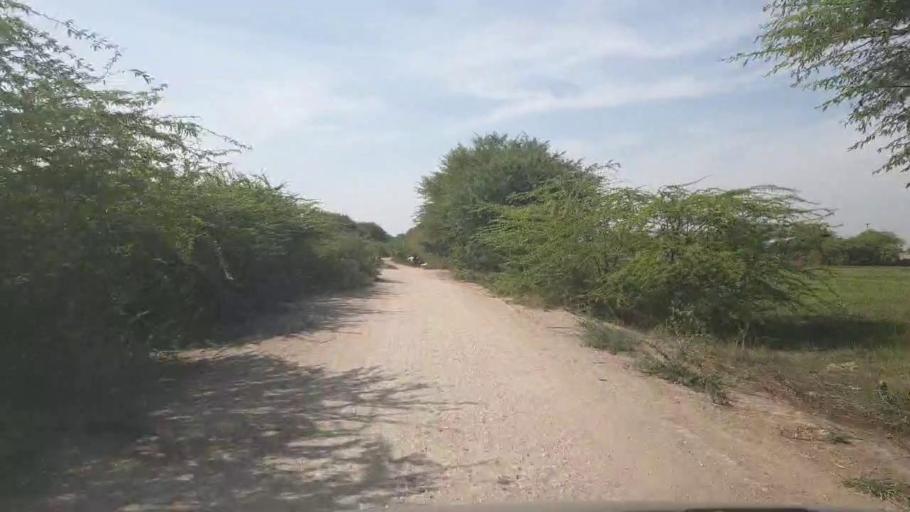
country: PK
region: Sindh
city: Kunri
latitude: 25.1836
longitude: 69.6713
